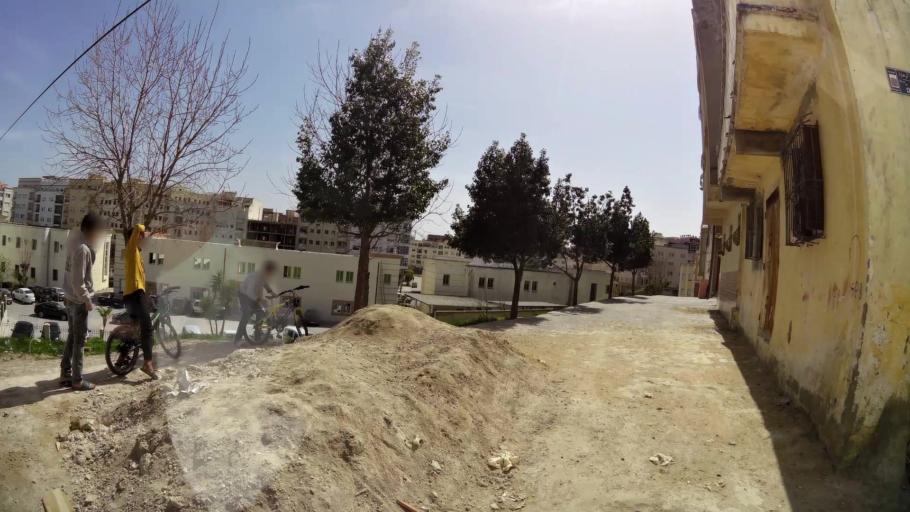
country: MA
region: Tanger-Tetouan
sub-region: Tanger-Assilah
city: Tangier
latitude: 35.7424
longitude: -5.8002
